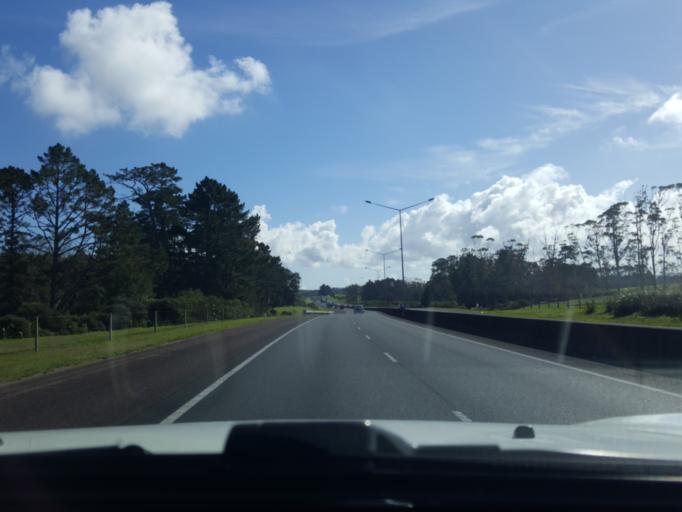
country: NZ
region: Auckland
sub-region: Auckland
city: Rosebank
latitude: -36.8046
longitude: 174.6049
